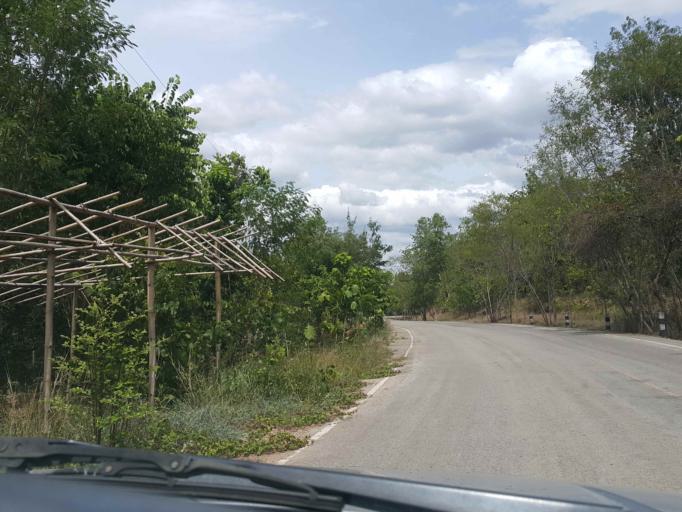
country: TH
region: Chiang Mai
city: Doi Lo
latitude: 18.5274
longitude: 98.7576
